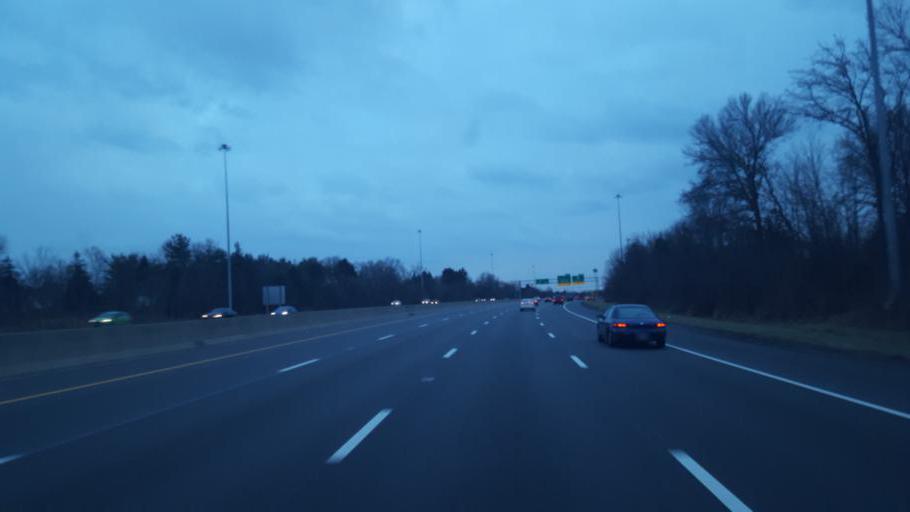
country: US
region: Ohio
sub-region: Franklin County
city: Reynoldsburg
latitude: 39.9647
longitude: -82.8430
